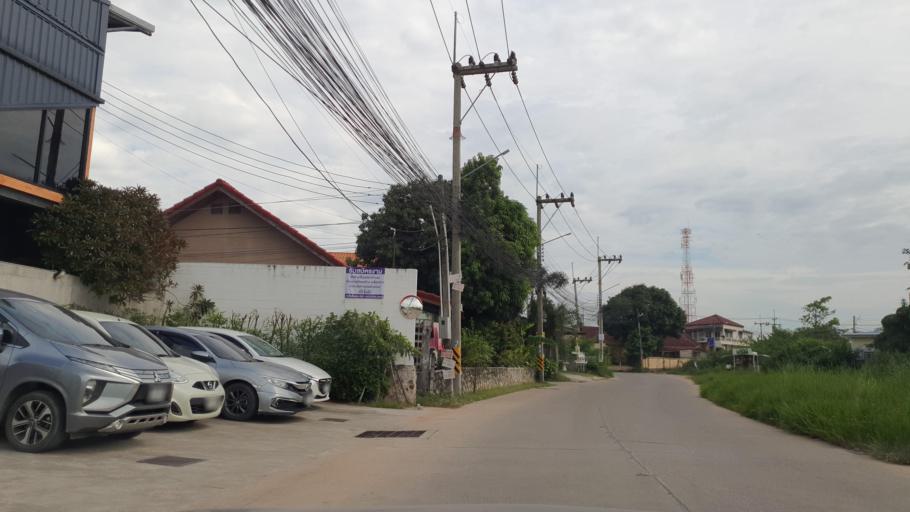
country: TH
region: Chon Buri
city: Phatthaya
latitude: 12.9550
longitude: 100.9198
